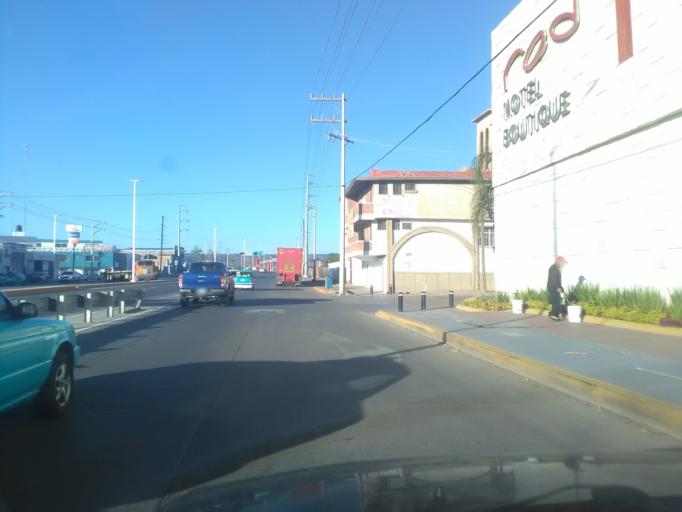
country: MX
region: Durango
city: Victoria de Durango
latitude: 24.0072
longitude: -104.6948
